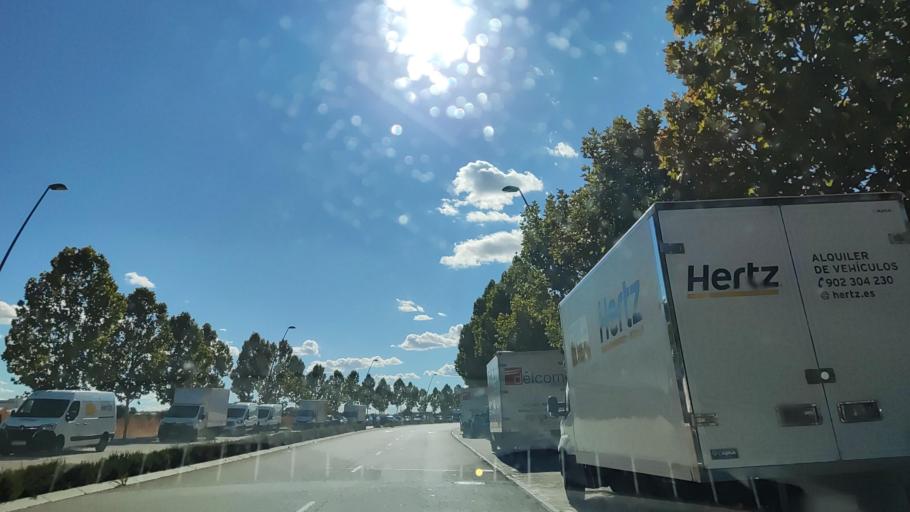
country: ES
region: Madrid
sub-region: Provincia de Madrid
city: Pinto
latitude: 40.2758
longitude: -3.6814
